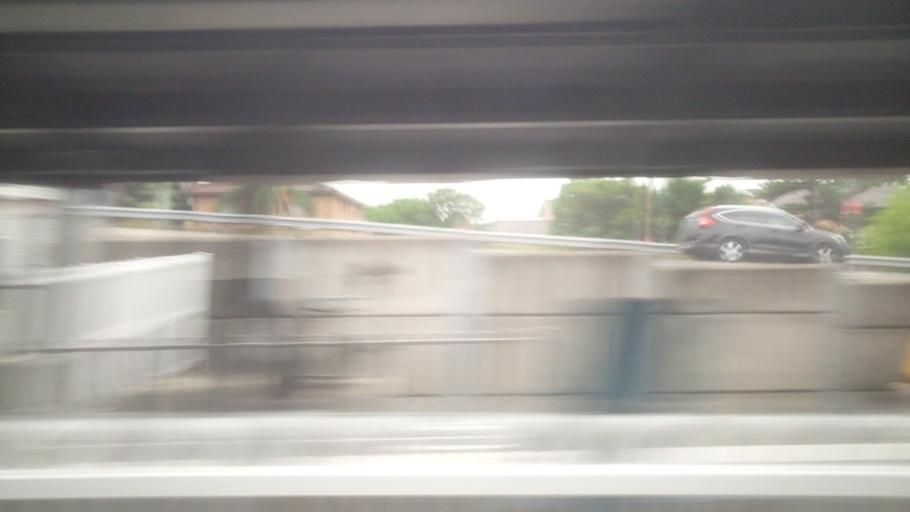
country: AU
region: New South Wales
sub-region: Auburn
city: Lidcombe
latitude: -33.8642
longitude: 151.0469
